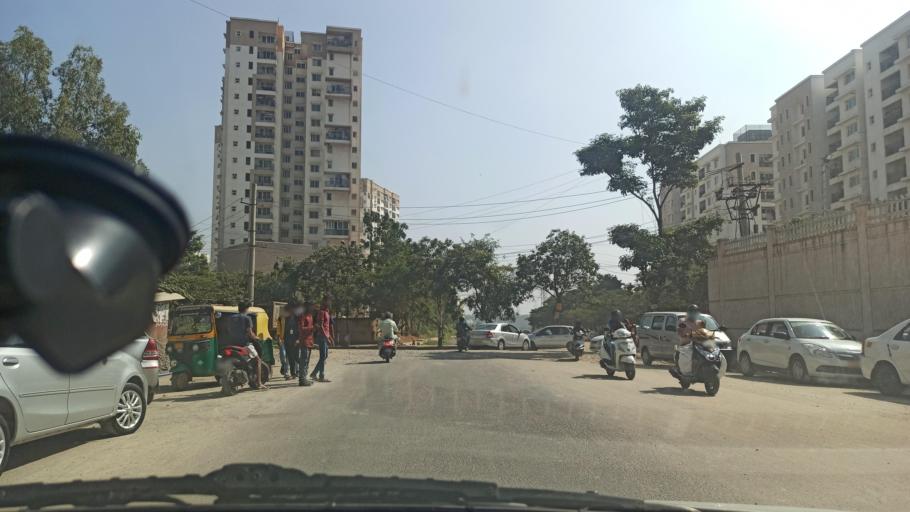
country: IN
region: Karnataka
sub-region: Bangalore Urban
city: Bangalore
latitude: 12.9313
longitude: 77.6947
